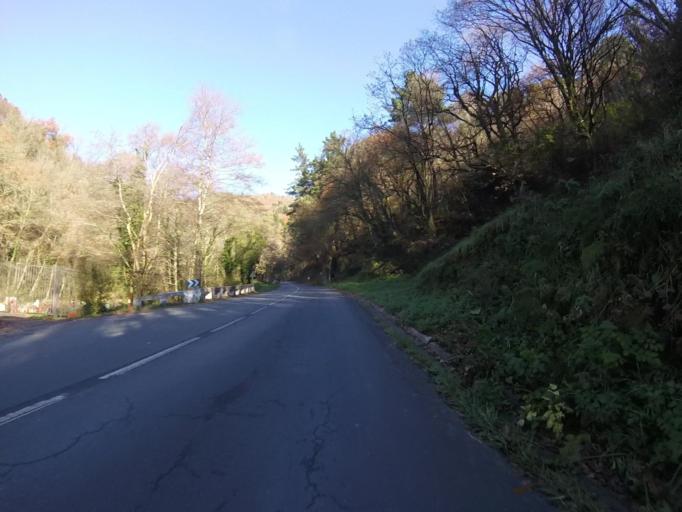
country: ES
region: Basque Country
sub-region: Provincia de Guipuzcoa
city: Lezo
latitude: 43.3260
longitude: -1.9098
